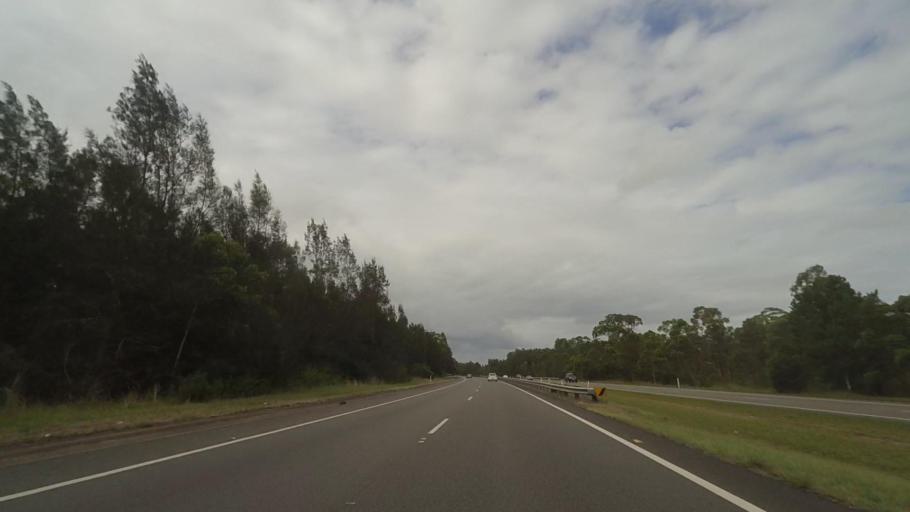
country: AU
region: New South Wales
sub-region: Port Stephens Shire
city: Raymond Terrace
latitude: -32.7720
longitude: 151.7597
